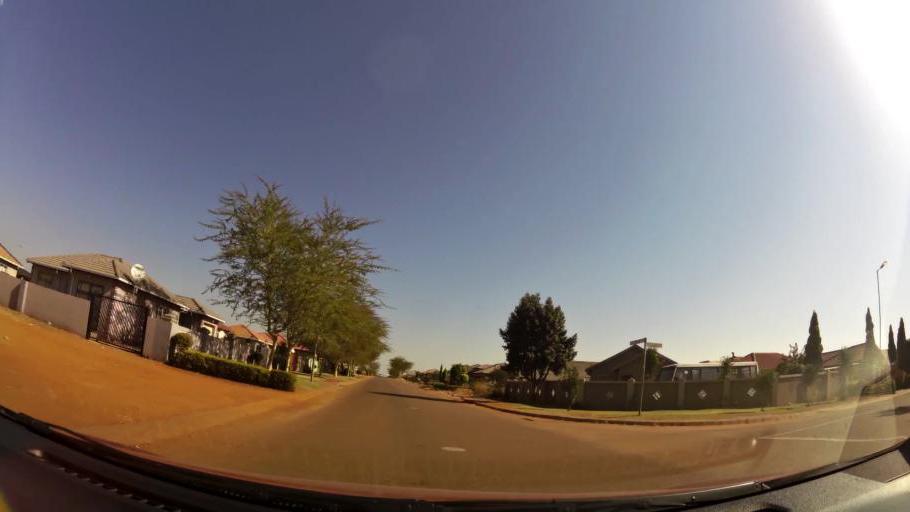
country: ZA
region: North-West
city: Ga-Rankuwa
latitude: -25.6355
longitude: 28.0786
